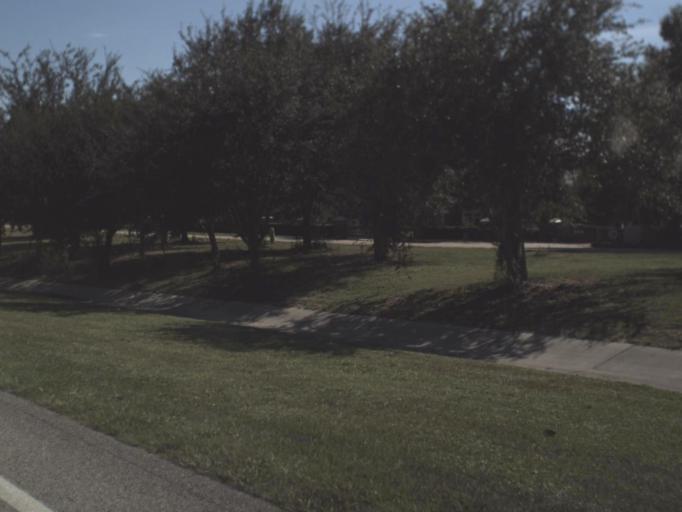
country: US
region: Florida
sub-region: Highlands County
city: Lake Placid
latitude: 27.3170
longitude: -81.3625
